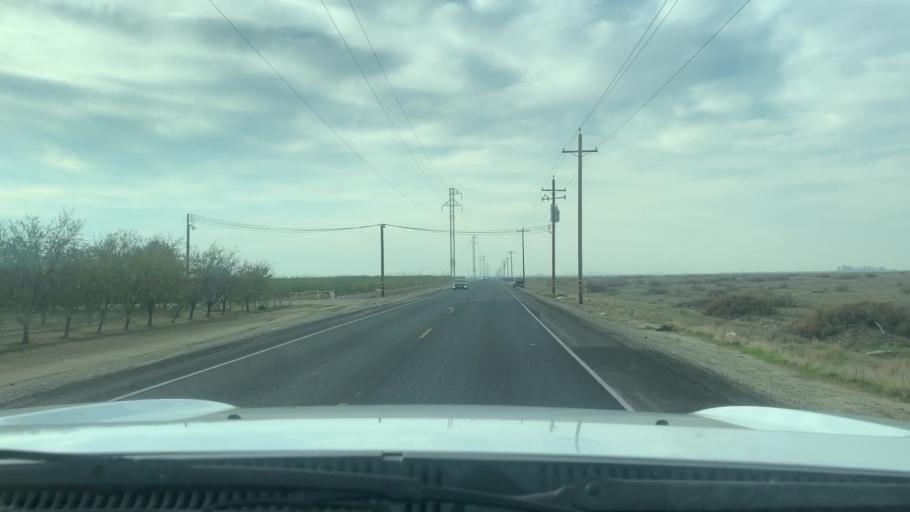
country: US
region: California
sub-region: Kern County
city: Shafter
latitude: 35.4420
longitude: -119.3534
